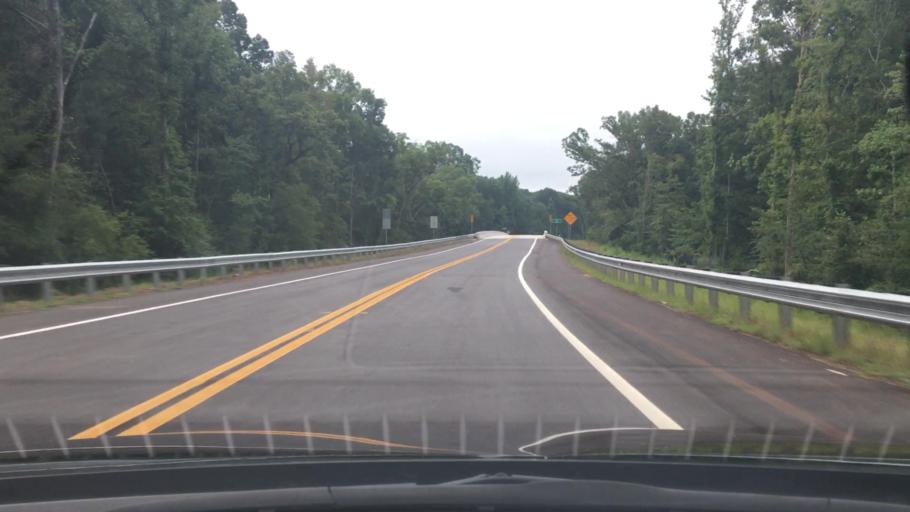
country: US
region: Georgia
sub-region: Fayette County
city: Shannon
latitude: 33.2835
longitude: -84.4261
